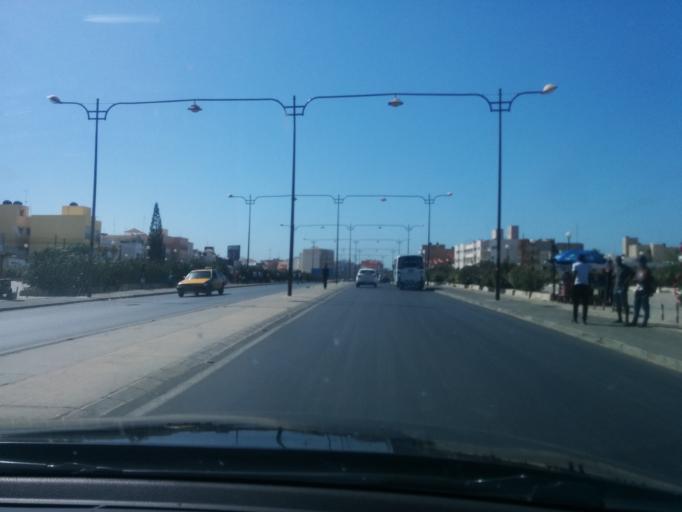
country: SN
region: Dakar
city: Grand Dakar
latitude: 14.7205
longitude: -17.4645
